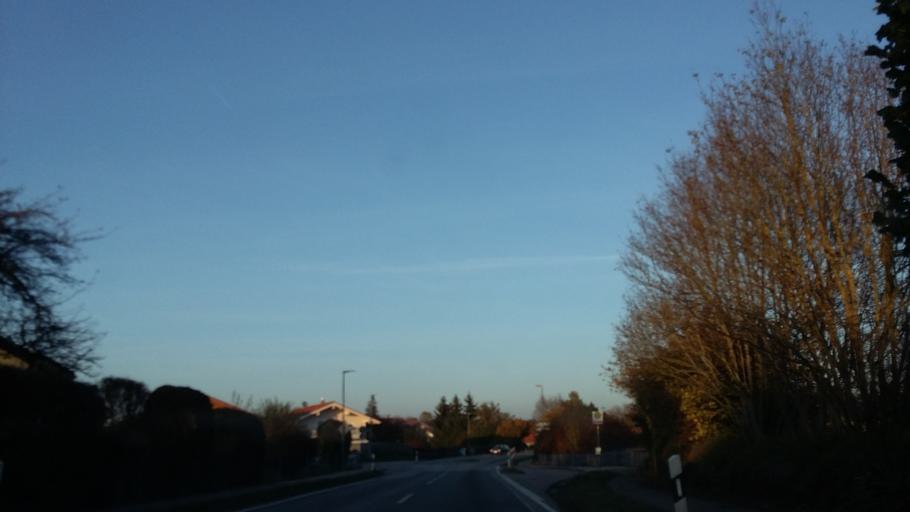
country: DE
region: Bavaria
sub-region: Upper Bavaria
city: Rimsting
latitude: 47.8879
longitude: 12.3414
